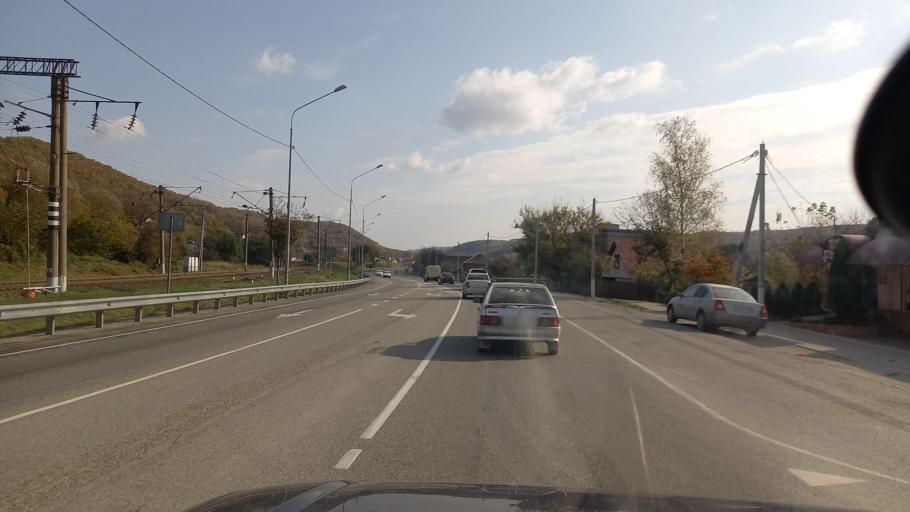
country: RU
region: Krasnodarskiy
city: Krymsk
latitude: 44.8687
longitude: 37.8721
